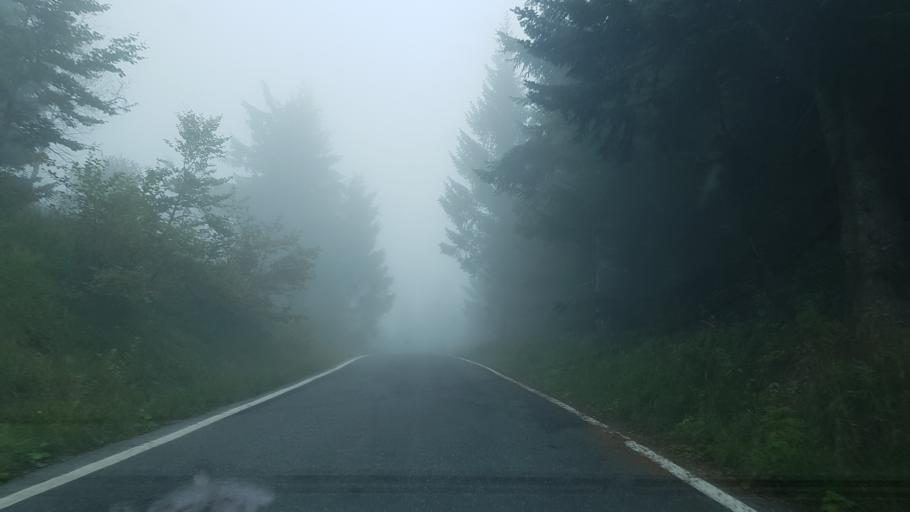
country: IT
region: Piedmont
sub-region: Provincia di Cuneo
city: Frabosa Soprana
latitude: 44.2579
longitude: 7.7927
